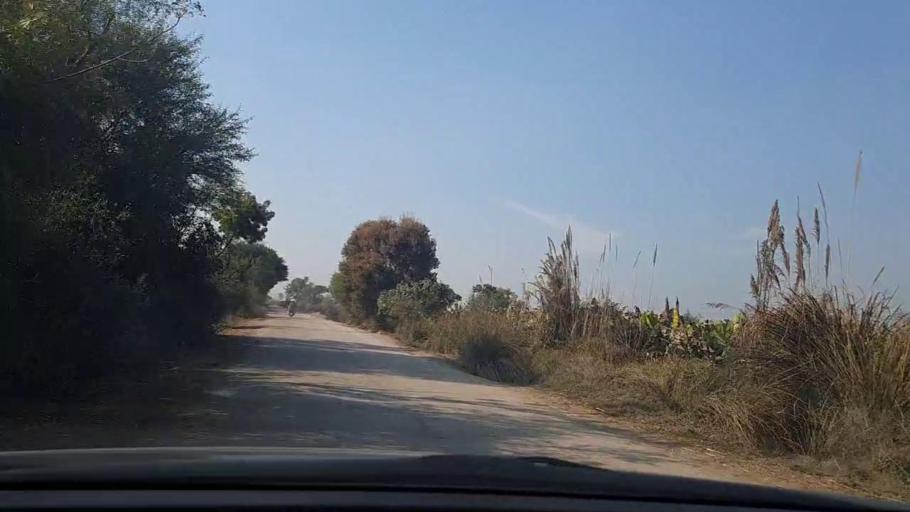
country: PK
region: Sindh
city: Daulatpur
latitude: 26.3066
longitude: 68.0860
